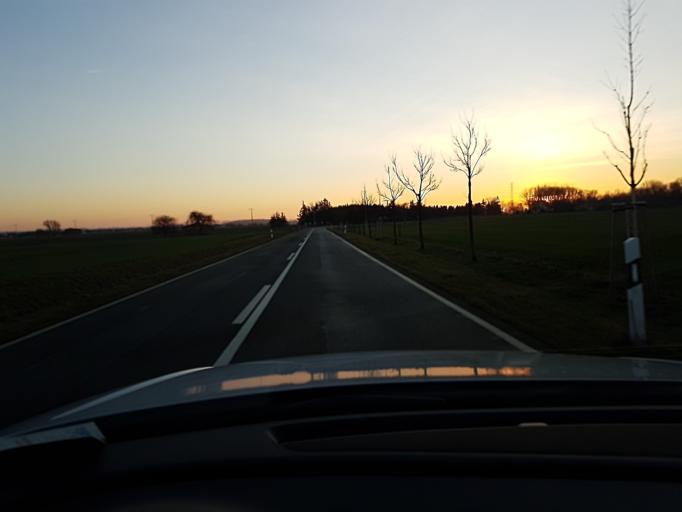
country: DE
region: Mecklenburg-Vorpommern
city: Wiek
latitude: 54.5720
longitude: 13.2644
